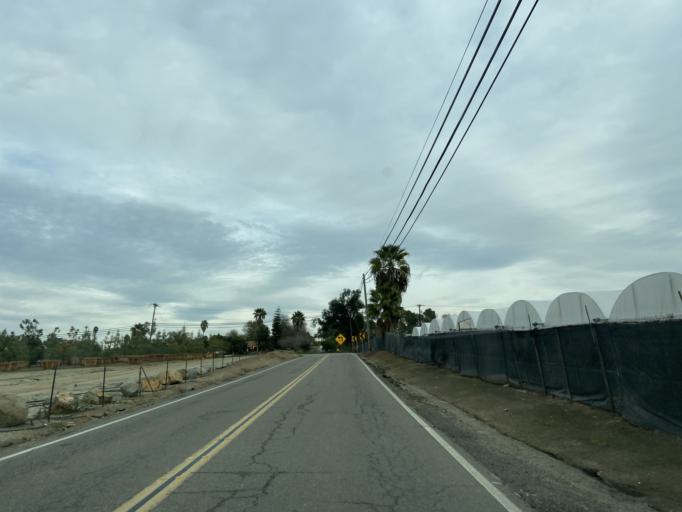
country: US
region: California
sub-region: San Diego County
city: Bonsall
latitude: 33.2634
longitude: -117.2464
